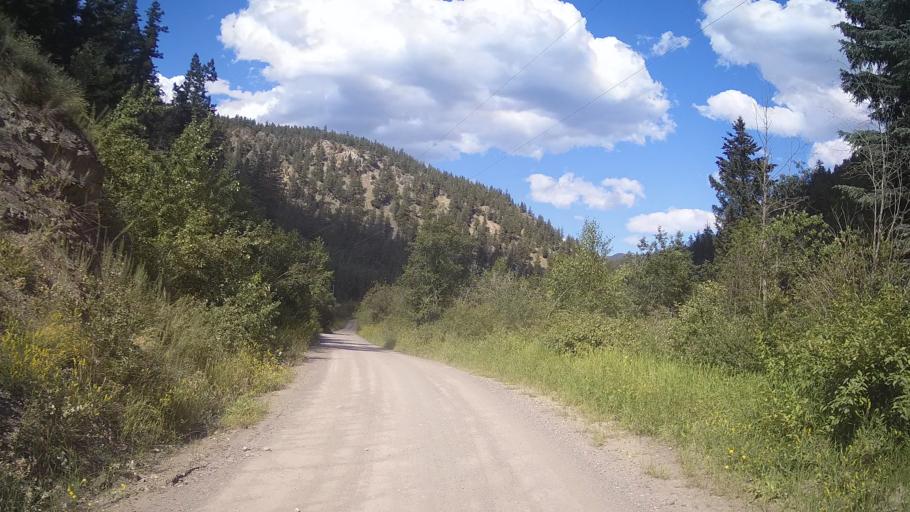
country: CA
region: British Columbia
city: Lillooet
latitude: 51.2559
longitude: -122.0014
